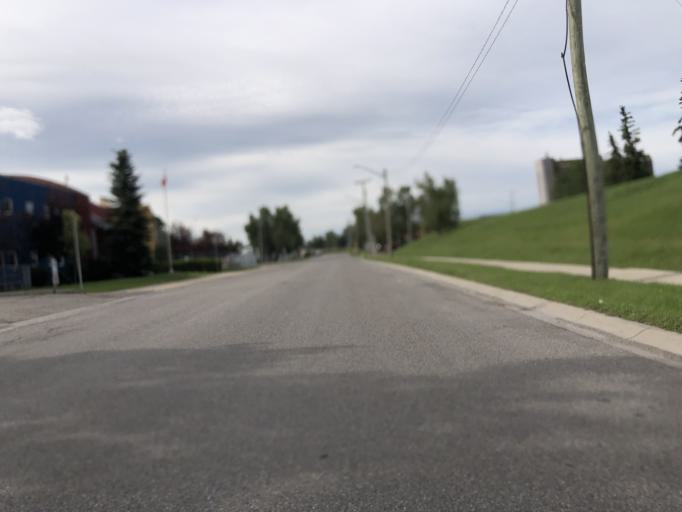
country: CA
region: Alberta
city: Calgary
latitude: 51.0700
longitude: -114.0091
